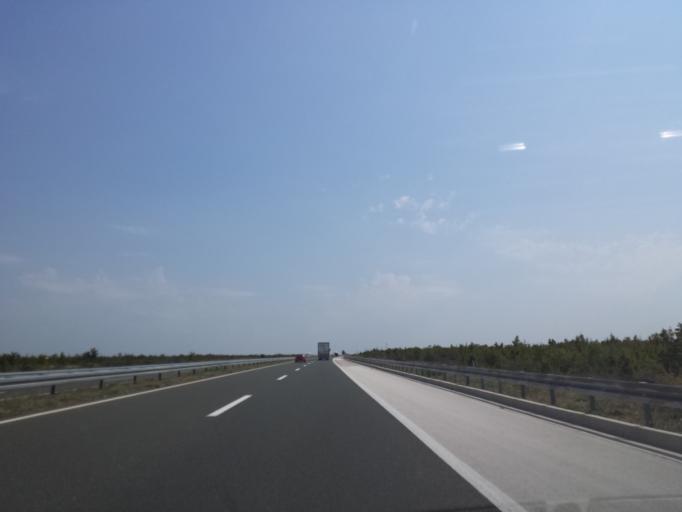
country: HR
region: Sibensko-Kniniska
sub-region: Grad Sibenik
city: Pirovac
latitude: 43.9231
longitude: 15.7319
